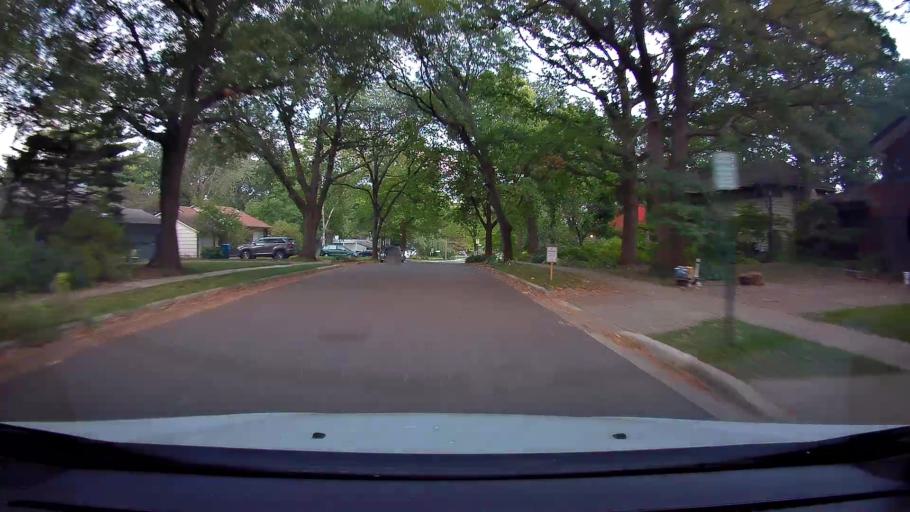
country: US
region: Minnesota
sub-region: Ramsey County
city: Lauderdale
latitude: 44.9895
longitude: -93.1941
